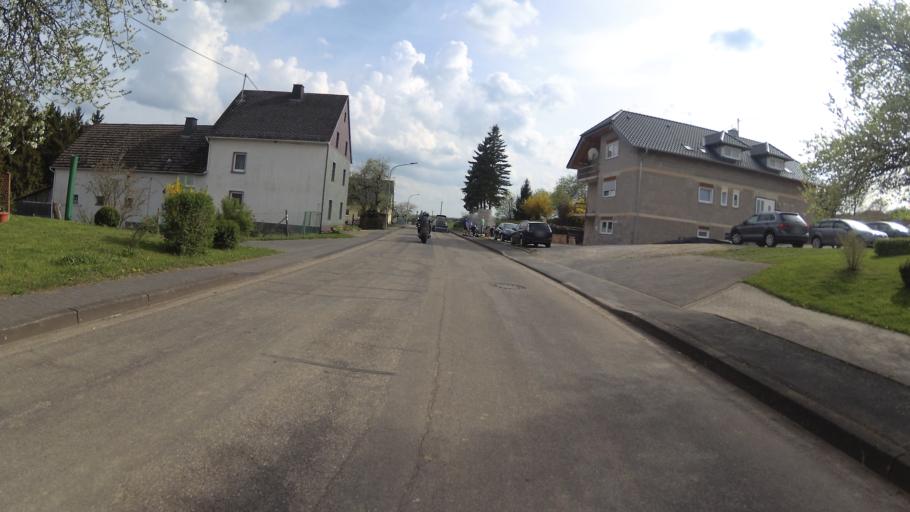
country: DE
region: Rheinland-Pfalz
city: Meuspath
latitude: 50.3426
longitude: 6.9740
